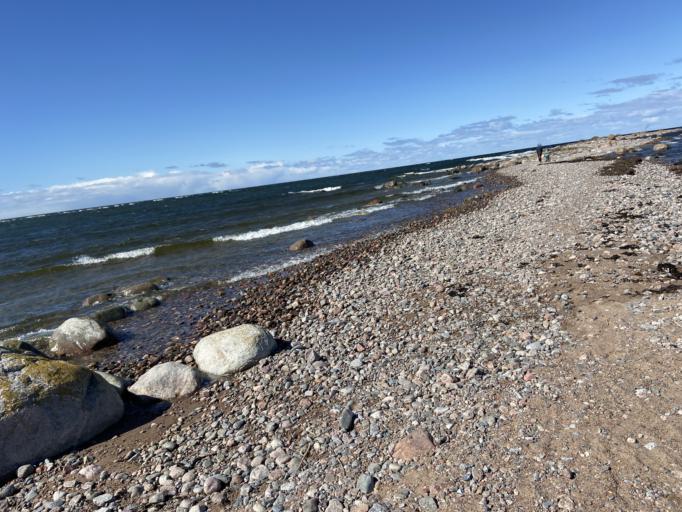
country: EE
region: Harju
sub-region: Loksa linn
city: Loksa
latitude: 59.6685
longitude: 25.6972
